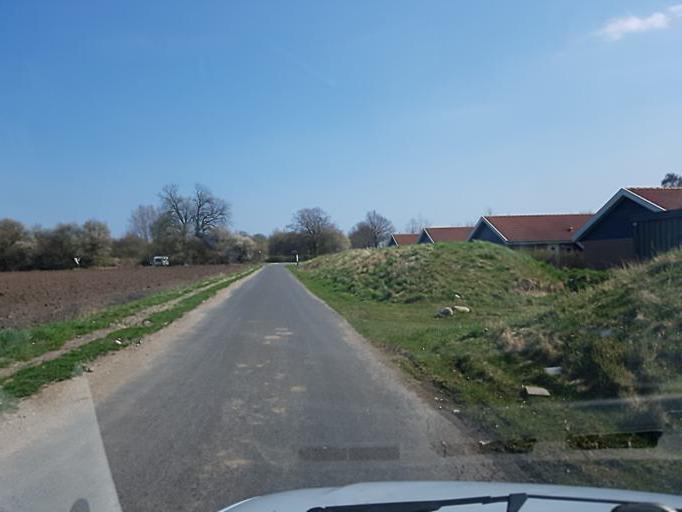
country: DK
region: South Denmark
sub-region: Odense Kommune
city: Neder Holluf
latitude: 55.3628
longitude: 10.4747
